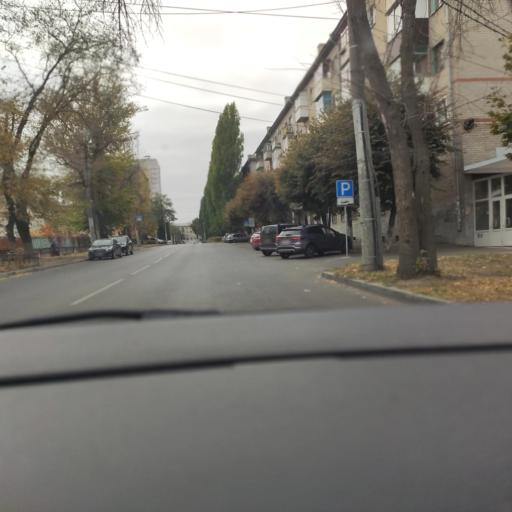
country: RU
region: Voronezj
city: Voronezh
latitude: 51.6803
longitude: 39.1908
